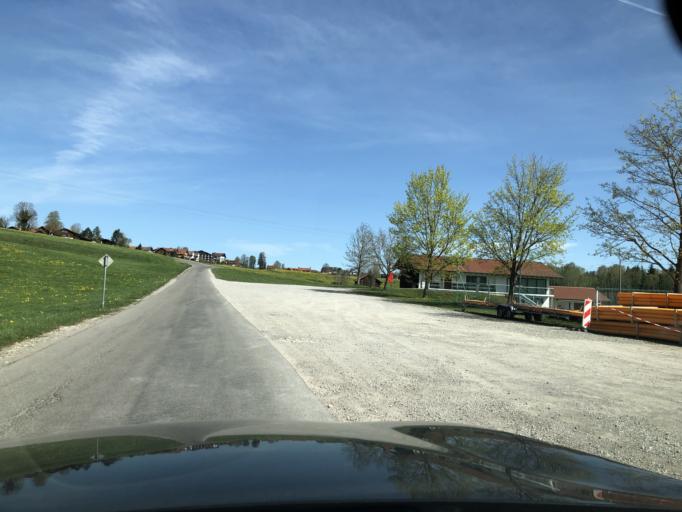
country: DE
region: Bavaria
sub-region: Swabia
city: Seeg
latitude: 47.6472
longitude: 10.6162
